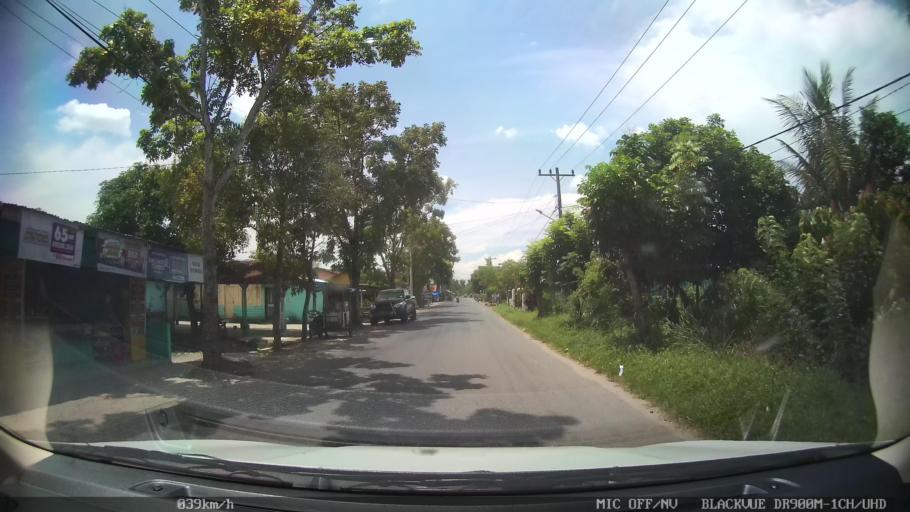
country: ID
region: North Sumatra
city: Binjai
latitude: 3.5929
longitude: 98.5183
